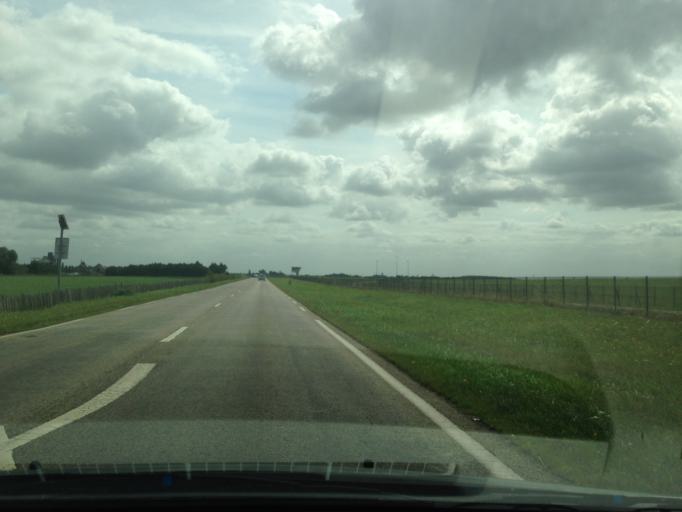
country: FR
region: Ile-de-France
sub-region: Departement du Val-d'Oise
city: Osny
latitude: 49.0988
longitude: 2.0459
